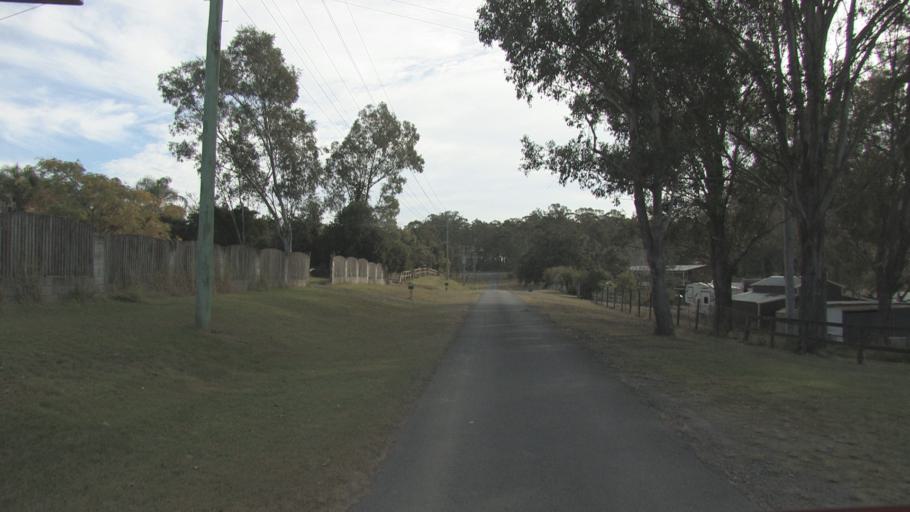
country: AU
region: Queensland
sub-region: Logan
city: Chambers Flat
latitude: -27.7487
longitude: 153.0621
